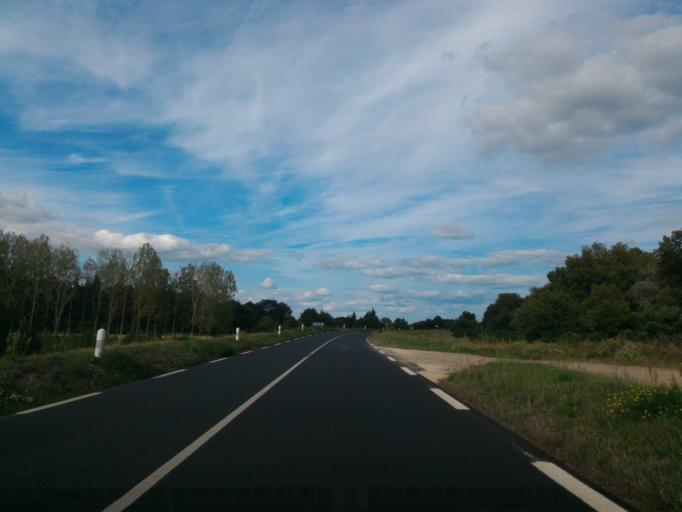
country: FR
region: Centre
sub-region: Departement du Loir-et-Cher
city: Chouzy-sur-Cisse
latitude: 47.5299
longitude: 1.2630
